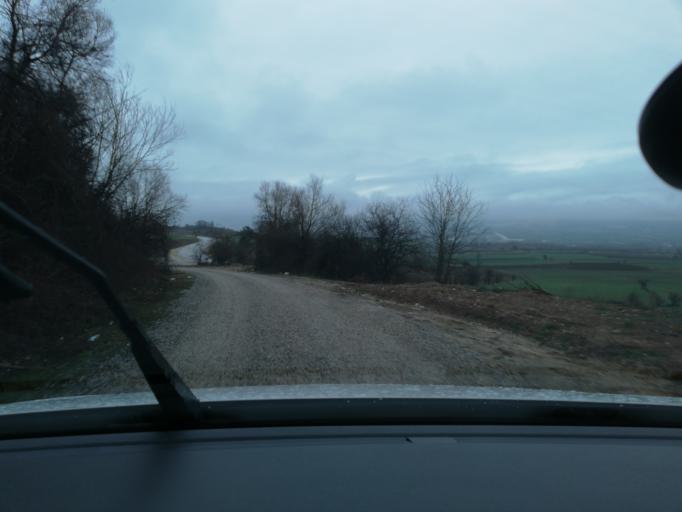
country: TR
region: Bolu
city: Bolu
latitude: 40.7647
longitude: 31.6528
